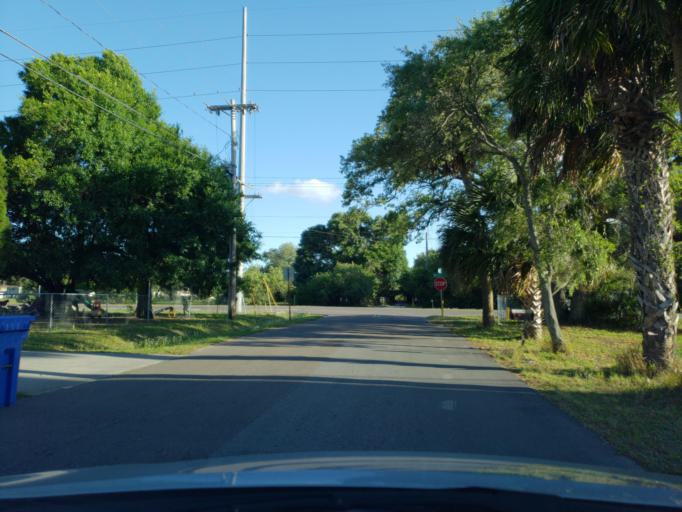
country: US
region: Florida
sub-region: Hillsborough County
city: Progress Village
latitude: 27.9014
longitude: -82.3810
